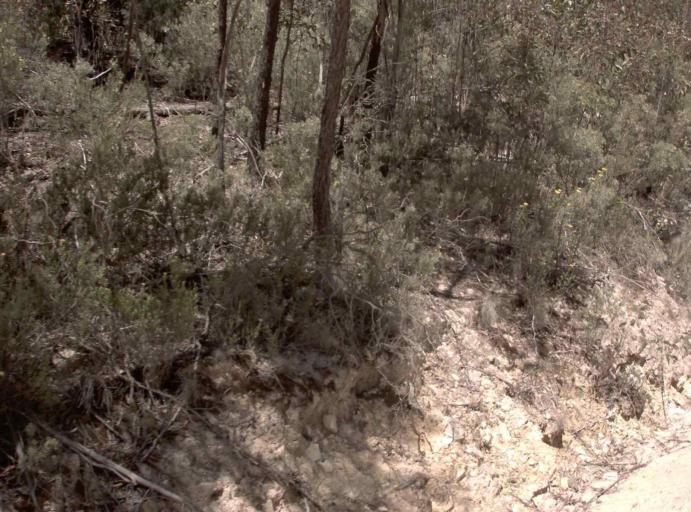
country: AU
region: New South Wales
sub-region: Snowy River
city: Jindabyne
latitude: -37.0866
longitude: 148.3272
